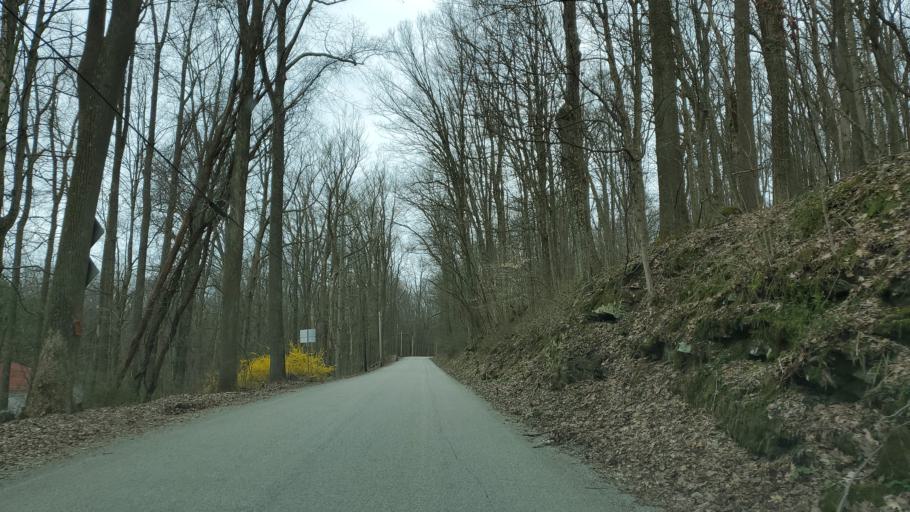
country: US
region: Pennsylvania
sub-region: Westmoreland County
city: Ligonier
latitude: 40.1821
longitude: -79.2393
